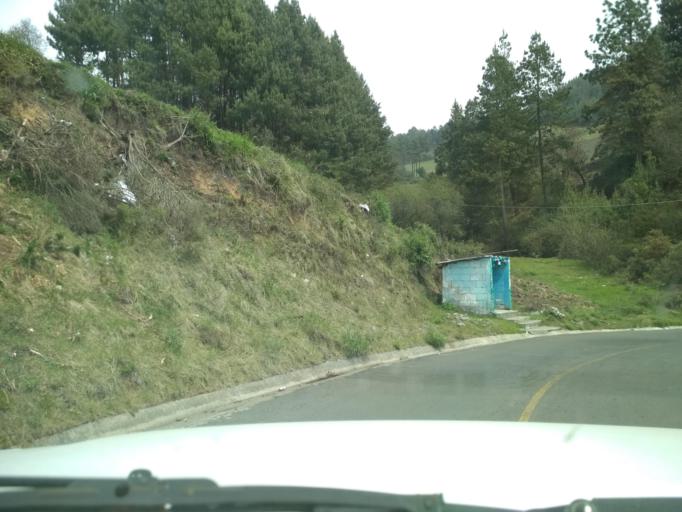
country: MX
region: Veracruz
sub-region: Mariano Escobedo
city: San Isidro el Berro
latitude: 18.9756
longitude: -97.2110
